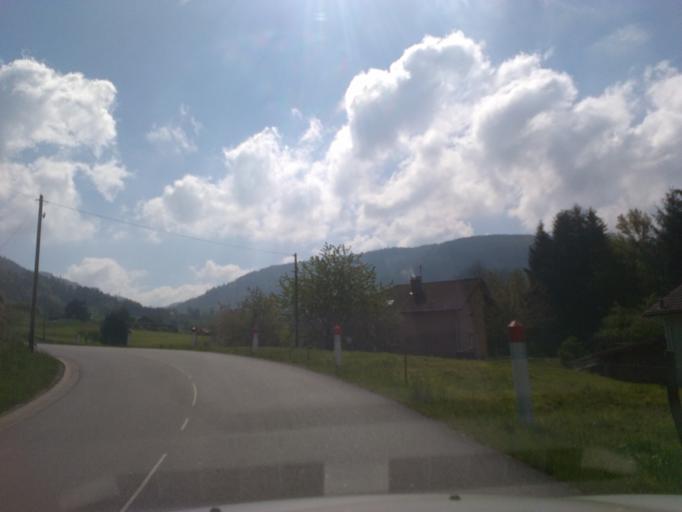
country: FR
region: Lorraine
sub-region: Departement des Vosges
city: Vagney
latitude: 47.9907
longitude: 6.7458
